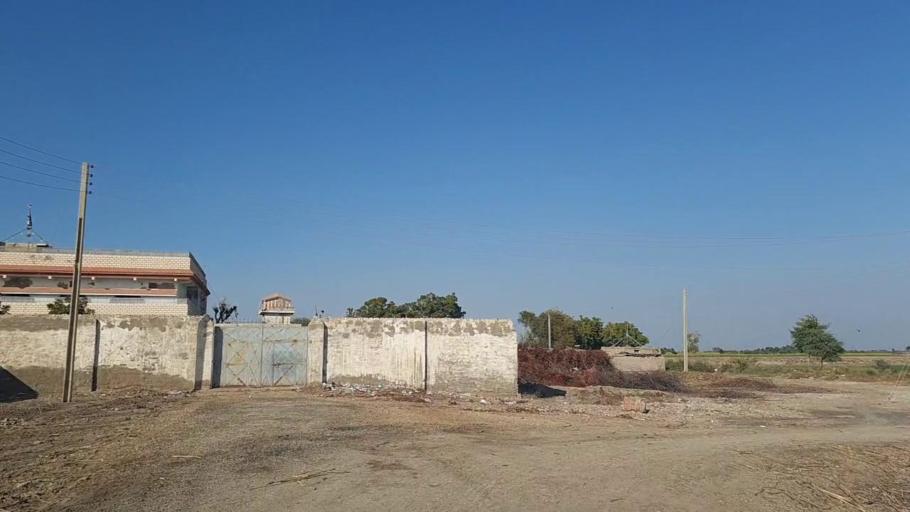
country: PK
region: Sindh
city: Shahpur Chakar
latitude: 26.2152
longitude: 68.6430
